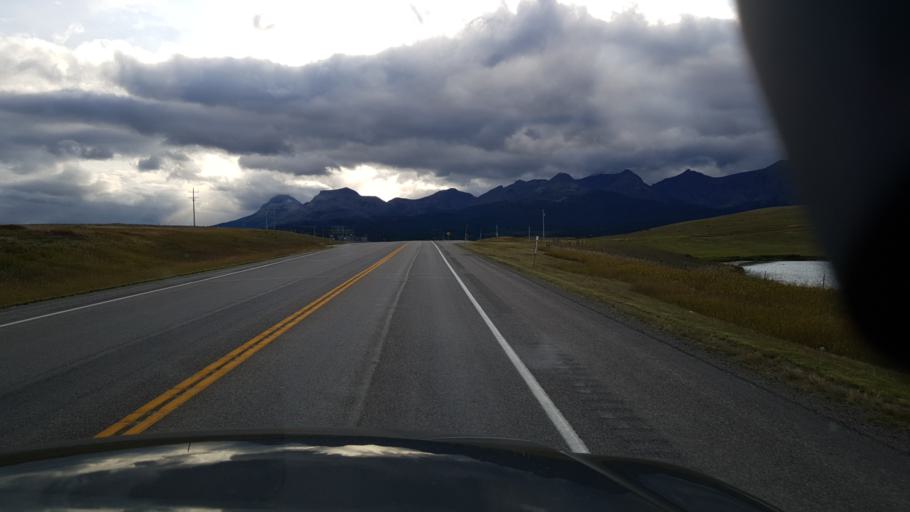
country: US
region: Montana
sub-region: Glacier County
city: South Browning
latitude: 48.4539
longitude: -113.1906
